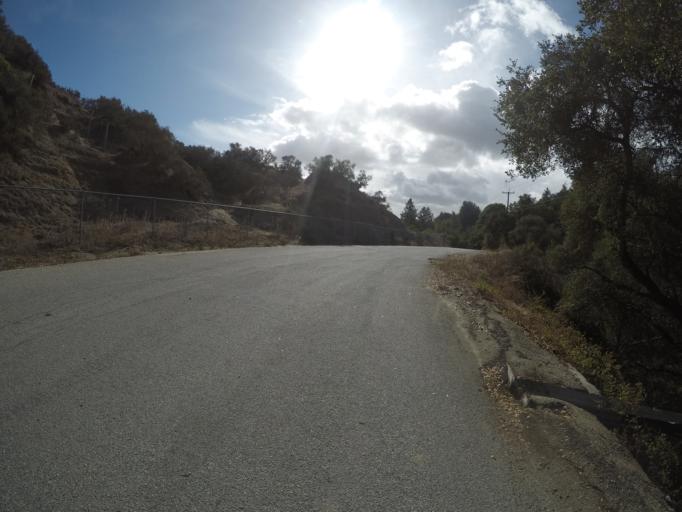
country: US
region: California
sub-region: Santa Cruz County
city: Scotts Valley
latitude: 37.0495
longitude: -121.9648
